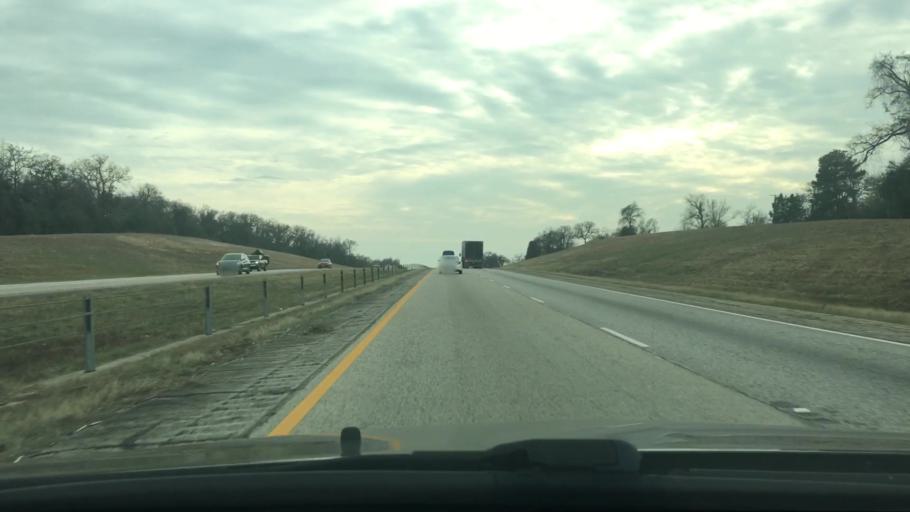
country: US
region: Texas
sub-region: Leon County
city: Centerville
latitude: 31.2255
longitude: -95.9953
